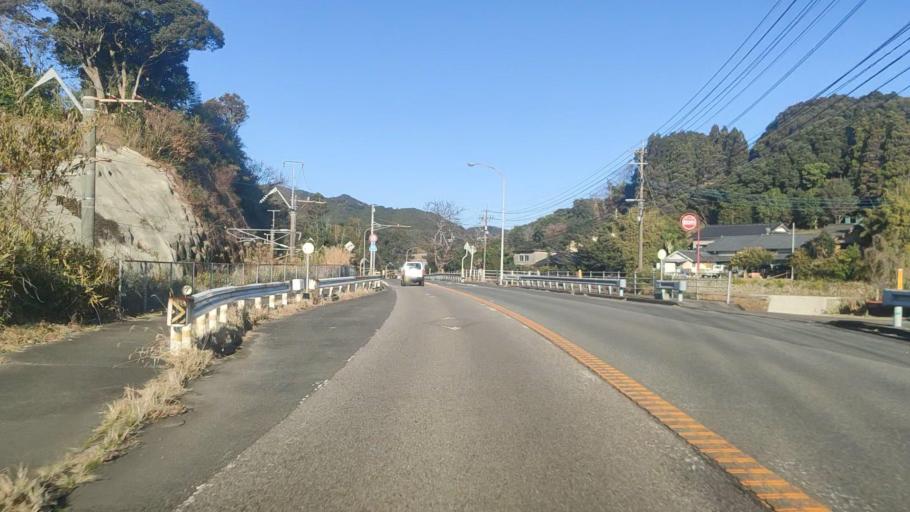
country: JP
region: Miyazaki
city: Nobeoka
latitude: 32.3763
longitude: 131.6296
